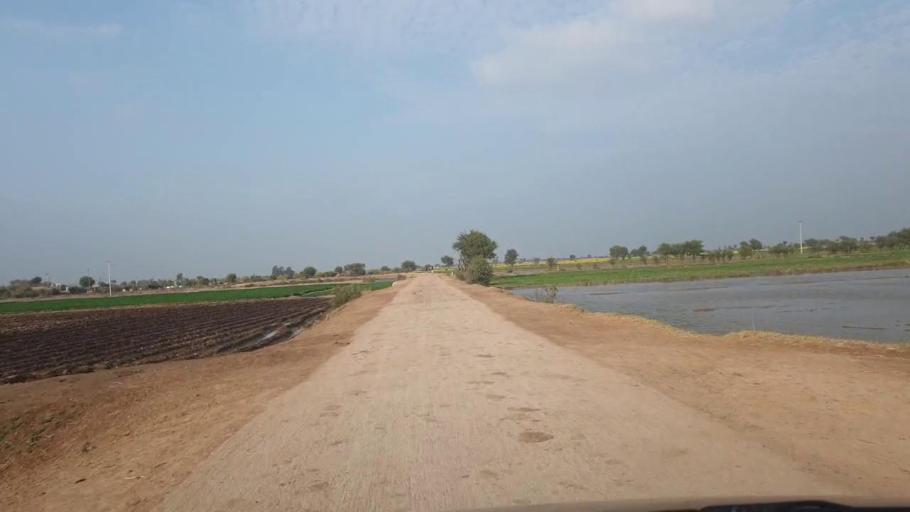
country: PK
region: Sindh
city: Shahdadpur
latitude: 25.8897
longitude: 68.7266
